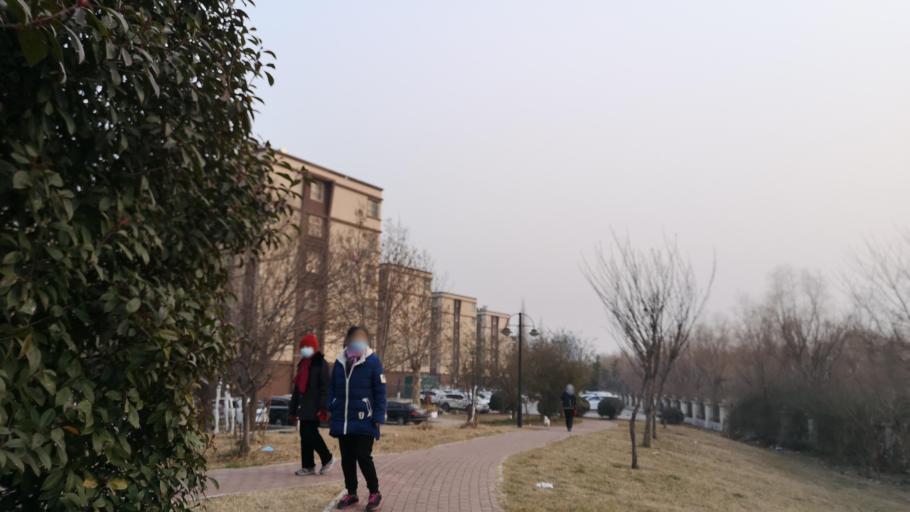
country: CN
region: Henan Sheng
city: Zhongyuanlu
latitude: 35.7885
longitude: 115.0750
